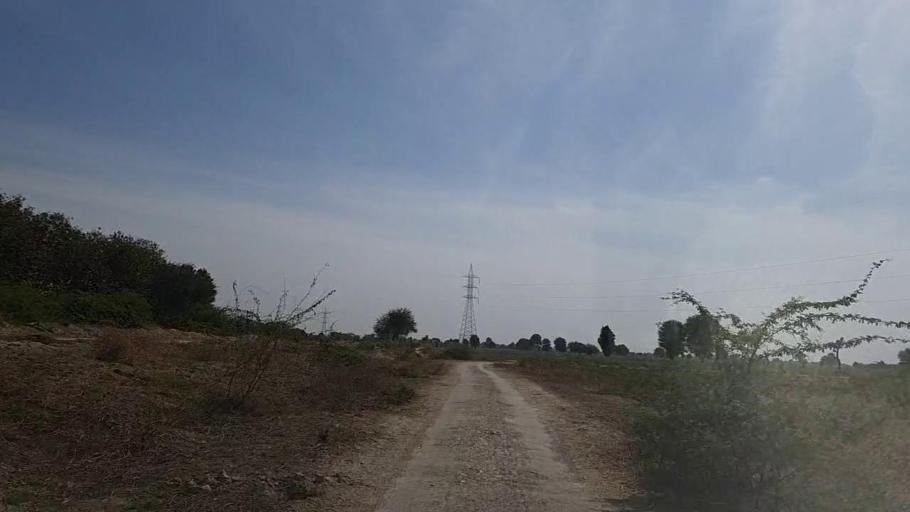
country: PK
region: Sindh
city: Samaro
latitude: 25.2080
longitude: 69.4564
